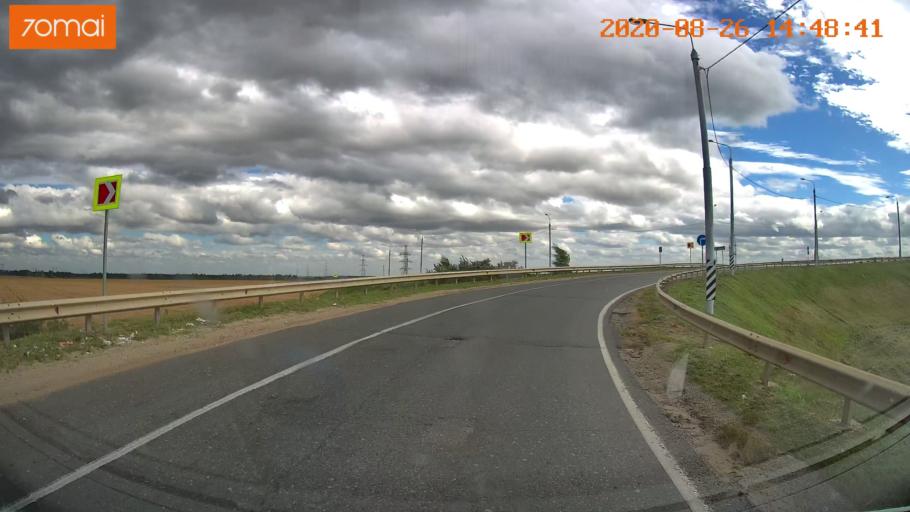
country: RU
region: Rjazan
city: Mikhaylov
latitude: 54.2638
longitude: 39.0063
